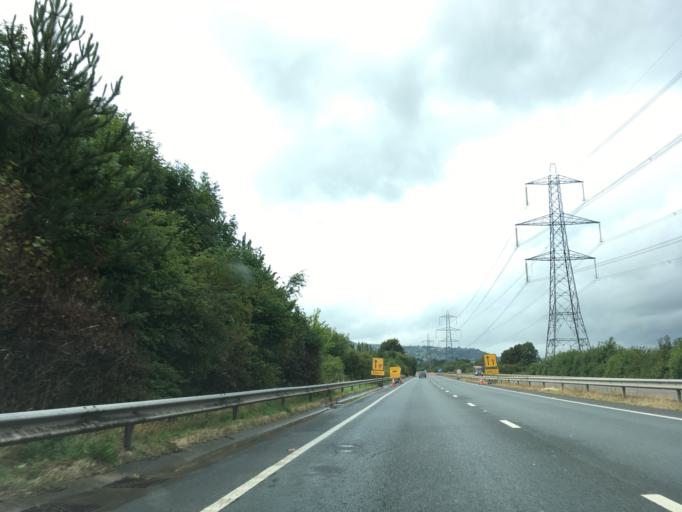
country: GB
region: Wales
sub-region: Monmouthshire
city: Gilwern
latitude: 51.8204
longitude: -3.0559
